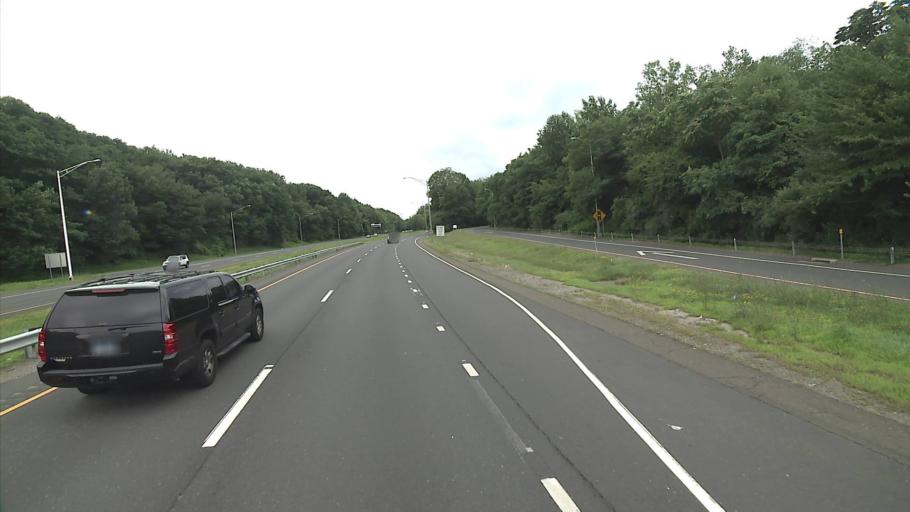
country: US
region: Connecticut
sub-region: Fairfield County
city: Shelton
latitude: 41.3035
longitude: -73.1002
